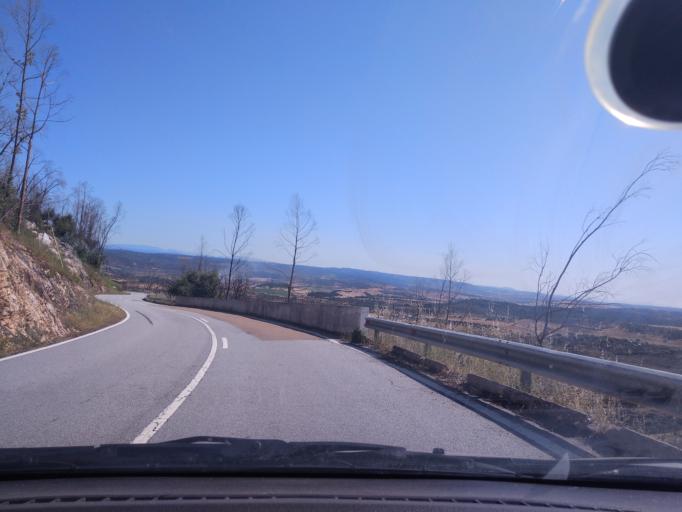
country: PT
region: Portalegre
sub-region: Nisa
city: Nisa
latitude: 39.6263
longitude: -7.6629
